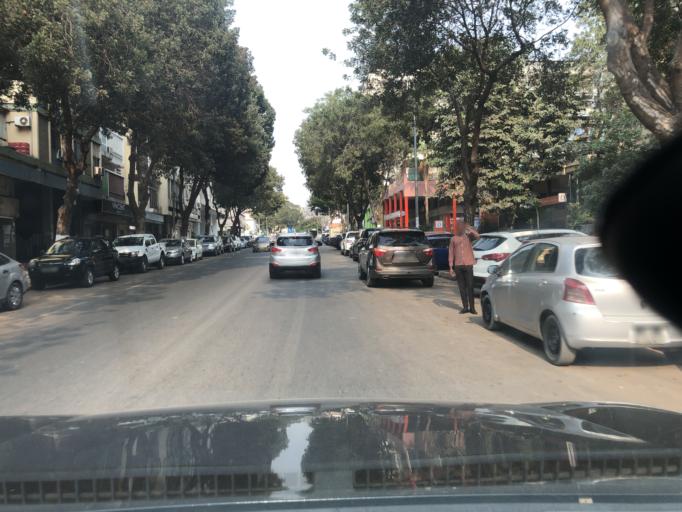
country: AO
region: Luanda
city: Luanda
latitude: -8.8191
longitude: 13.2439
